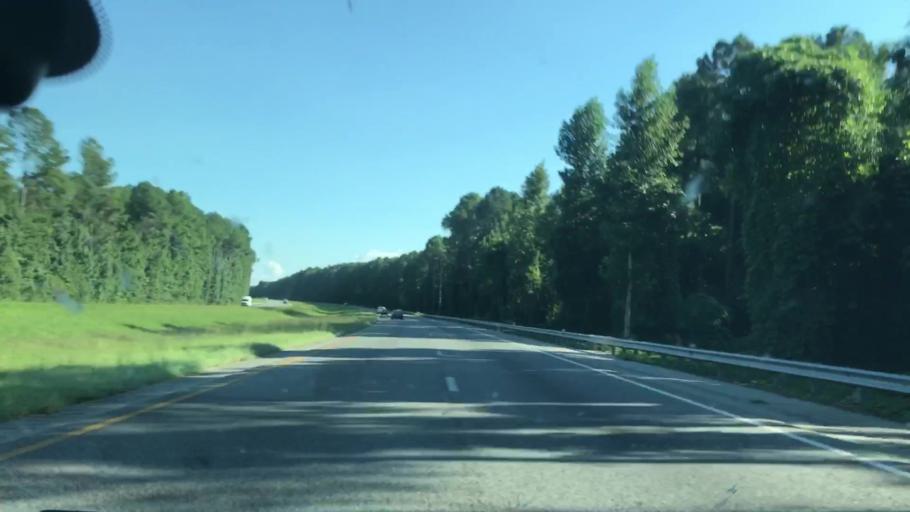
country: US
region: Georgia
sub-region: Harris County
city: Hamilton
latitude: 32.7735
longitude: -85.0211
